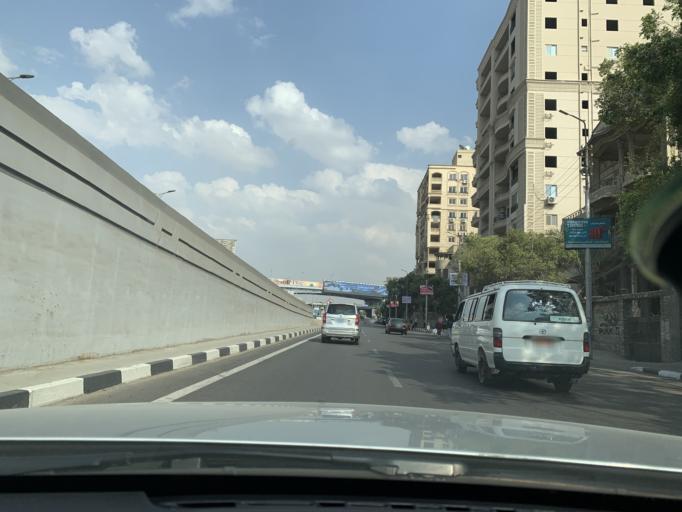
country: EG
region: Muhafazat al Qahirah
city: Cairo
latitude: 30.0969
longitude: 31.3394
